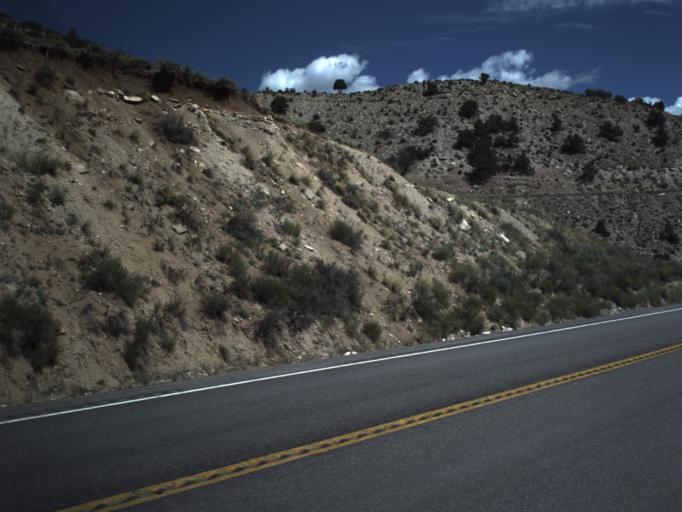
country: US
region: Utah
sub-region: Carbon County
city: Helper
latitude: 39.8100
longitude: -110.9419
